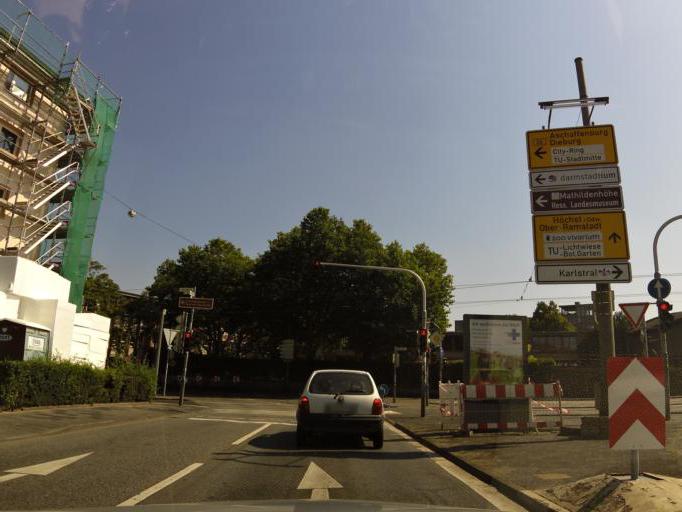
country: DE
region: Hesse
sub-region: Regierungsbezirk Darmstadt
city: Darmstadt
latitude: 49.8699
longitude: 8.6563
